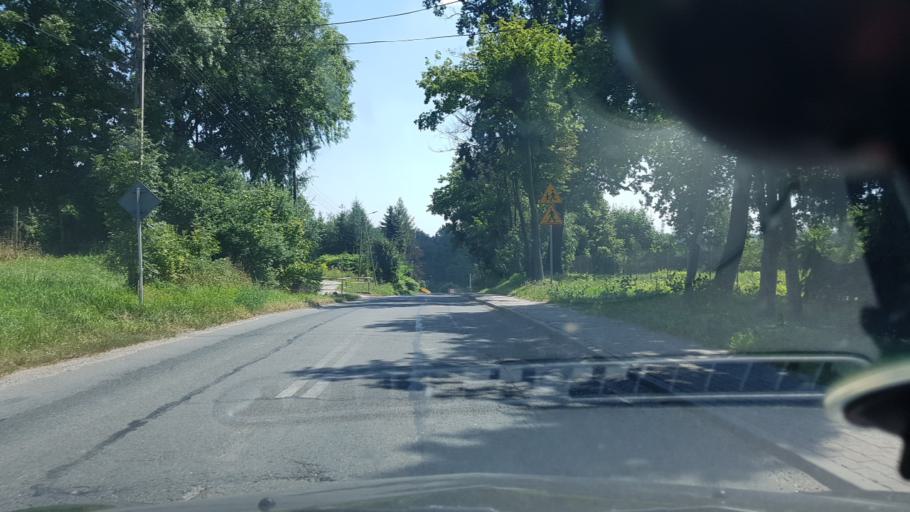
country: PL
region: Silesian Voivodeship
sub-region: Powiat wodzislawski
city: Marklowice
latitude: 50.0165
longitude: 18.5359
